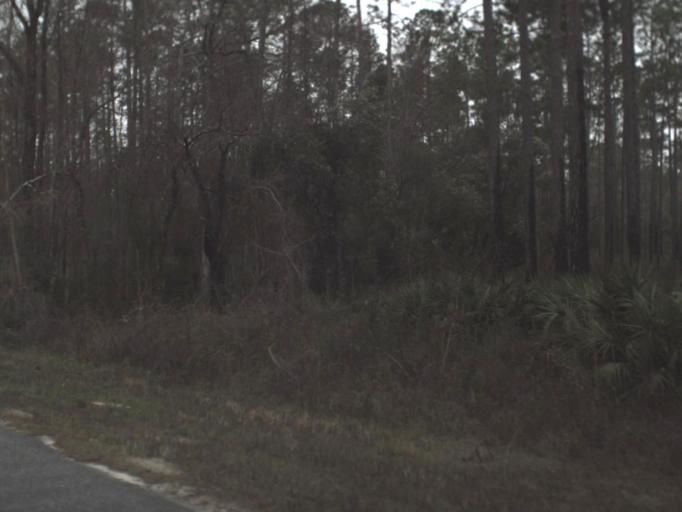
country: US
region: Florida
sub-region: Franklin County
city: Apalachicola
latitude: 29.9150
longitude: -84.9775
